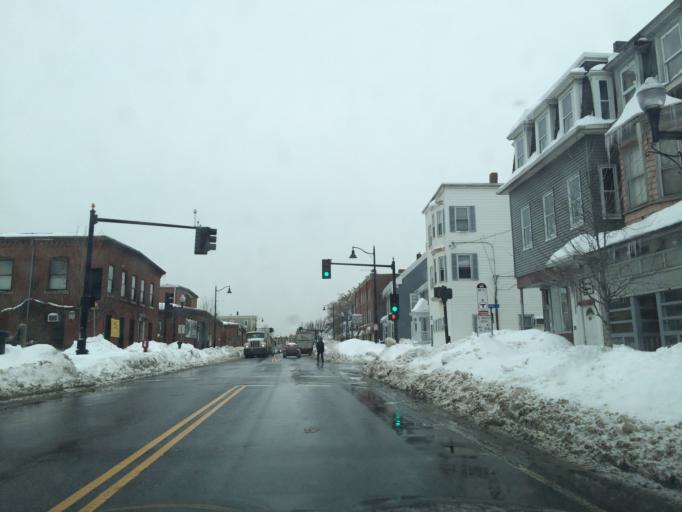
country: US
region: Massachusetts
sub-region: Middlesex County
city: Somerville
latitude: 42.3819
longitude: -71.1017
